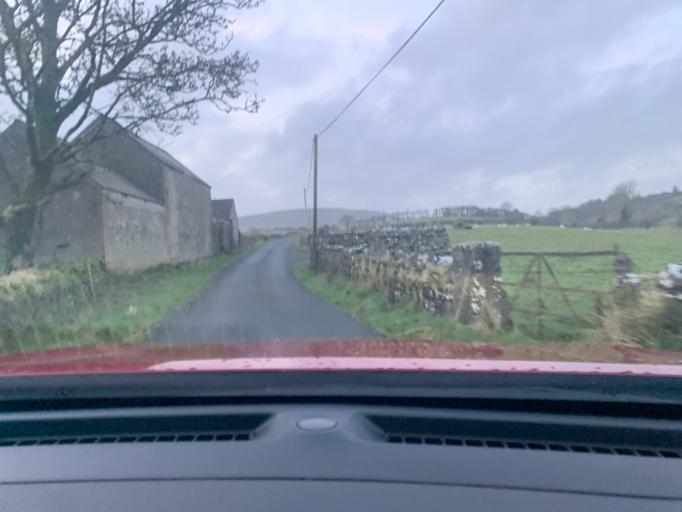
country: IE
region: Connaught
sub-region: Sligo
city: Ballymote
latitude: 54.0381
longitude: -8.4073
